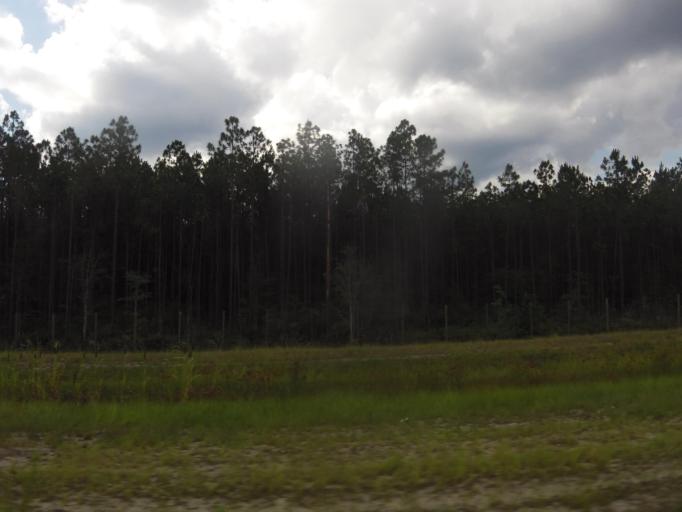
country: US
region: Florida
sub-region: Duval County
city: Baldwin
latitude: 30.3129
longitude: -81.9808
